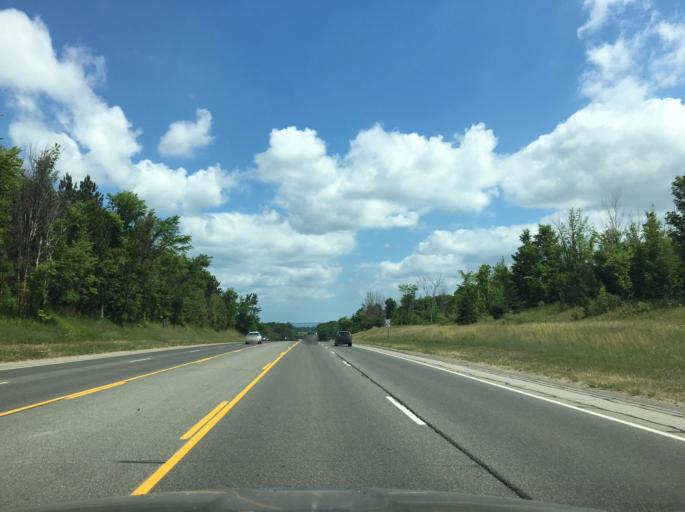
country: US
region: Michigan
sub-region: Grand Traverse County
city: Traverse City
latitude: 44.7029
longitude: -85.6549
